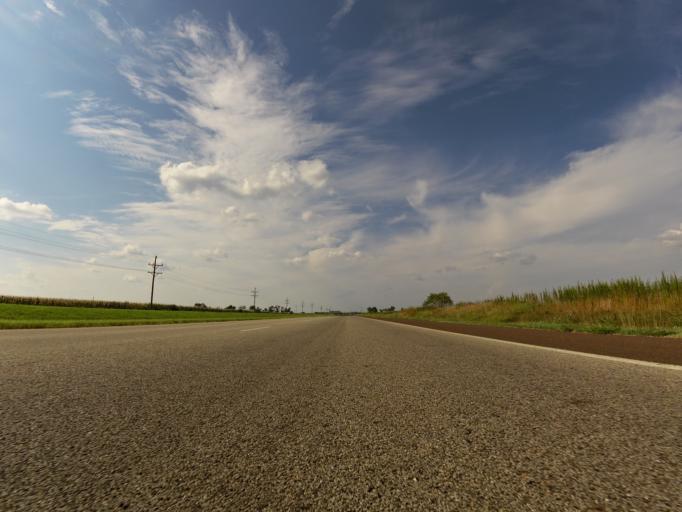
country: US
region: Kansas
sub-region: Reno County
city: South Hutchinson
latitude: 37.9959
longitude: -97.9401
